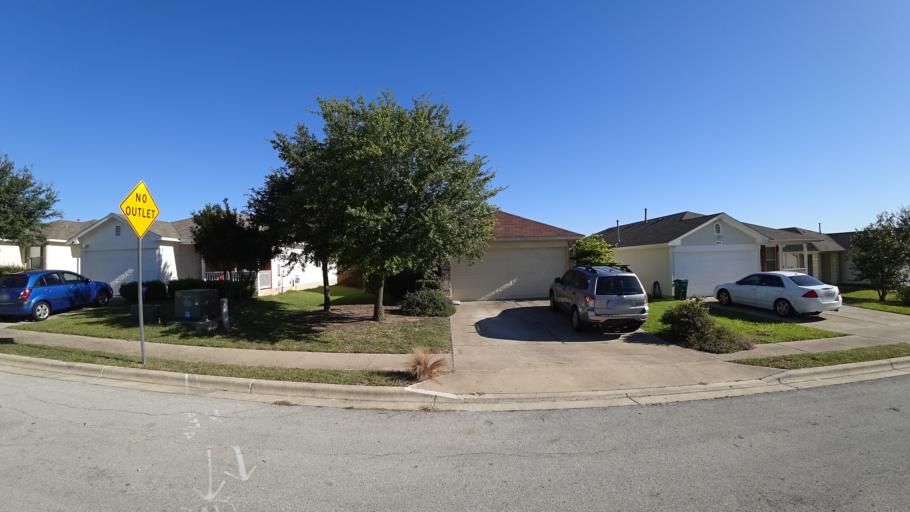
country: US
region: Texas
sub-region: Travis County
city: Austin
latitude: 30.2921
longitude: -97.6690
